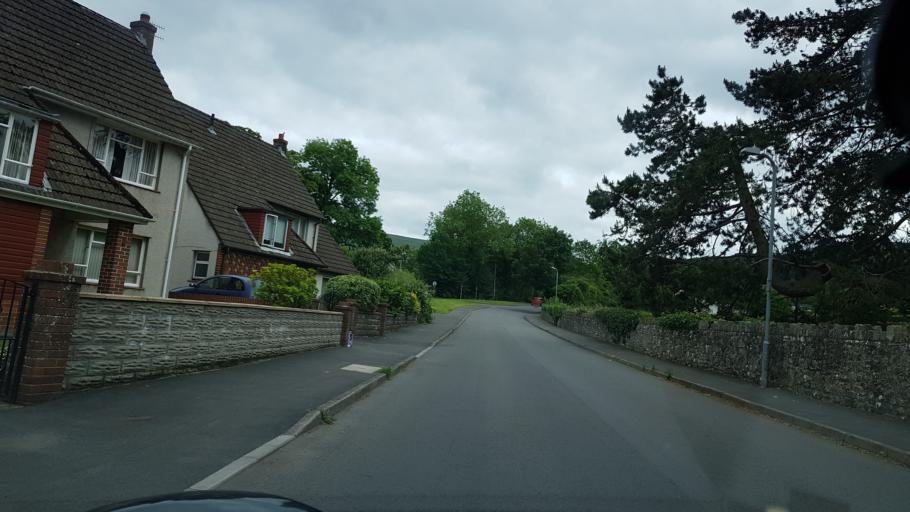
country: GB
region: Wales
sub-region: Monmouthshire
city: Gilwern
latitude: 51.8304
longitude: -3.0936
